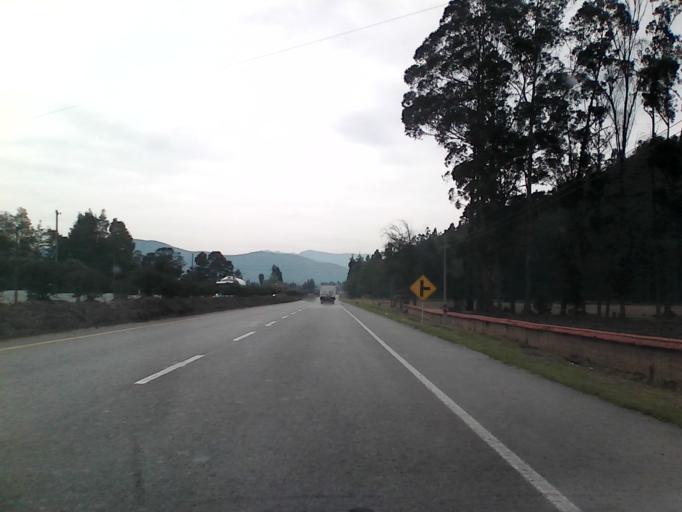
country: CO
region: Boyaca
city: Duitama
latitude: 5.8032
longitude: -73.0053
